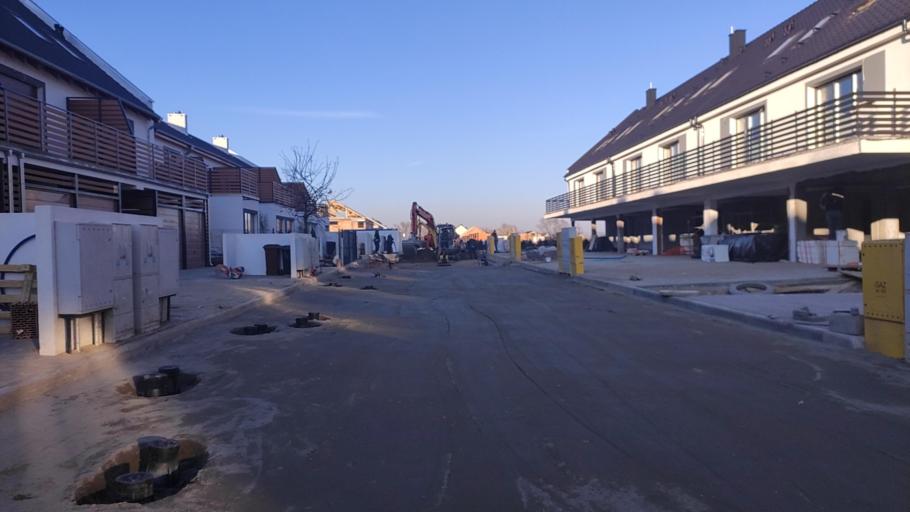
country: PL
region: Greater Poland Voivodeship
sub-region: Powiat poznanski
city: Kornik
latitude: 52.2965
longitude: 17.0843
